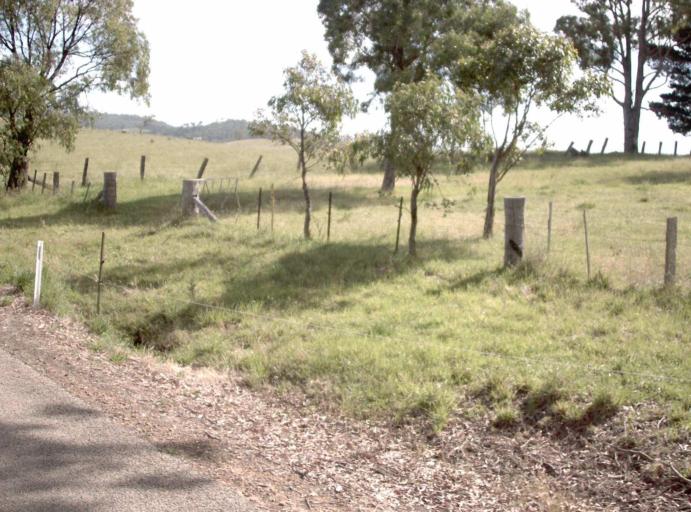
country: AU
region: Victoria
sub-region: East Gippsland
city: Lakes Entrance
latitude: -37.5039
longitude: 148.1332
